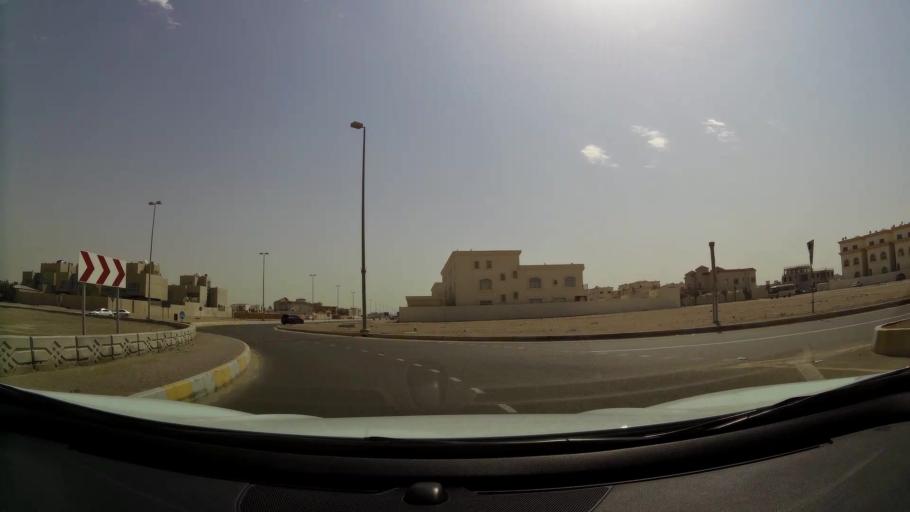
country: AE
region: Abu Dhabi
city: Abu Dhabi
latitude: 24.3319
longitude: 54.5512
